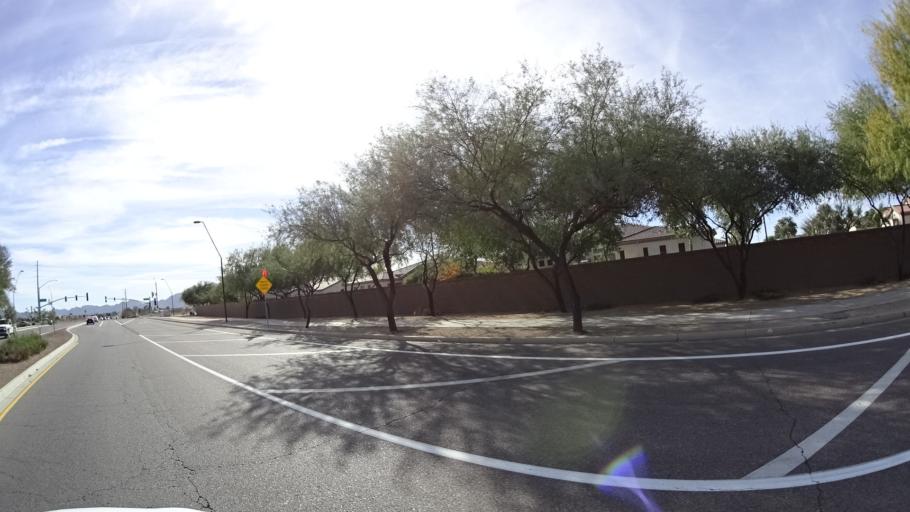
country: US
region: Arizona
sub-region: Maricopa County
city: Queen Creek
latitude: 33.2507
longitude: -111.6859
